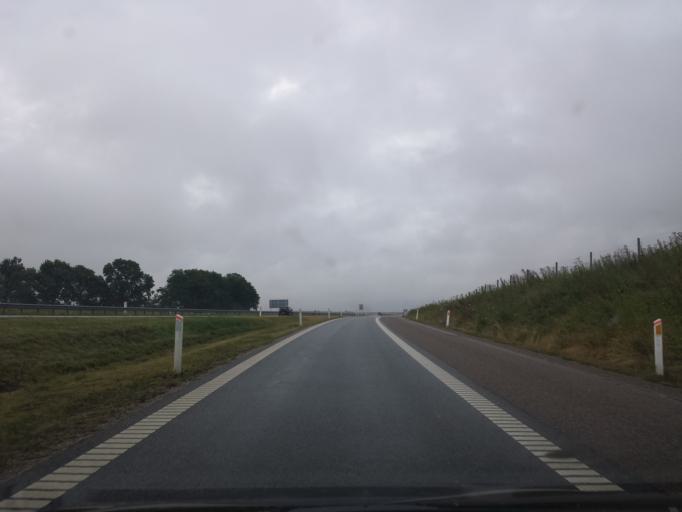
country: DK
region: South Denmark
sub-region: Sonderborg Kommune
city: Grasten
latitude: 54.9501
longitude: 9.6411
